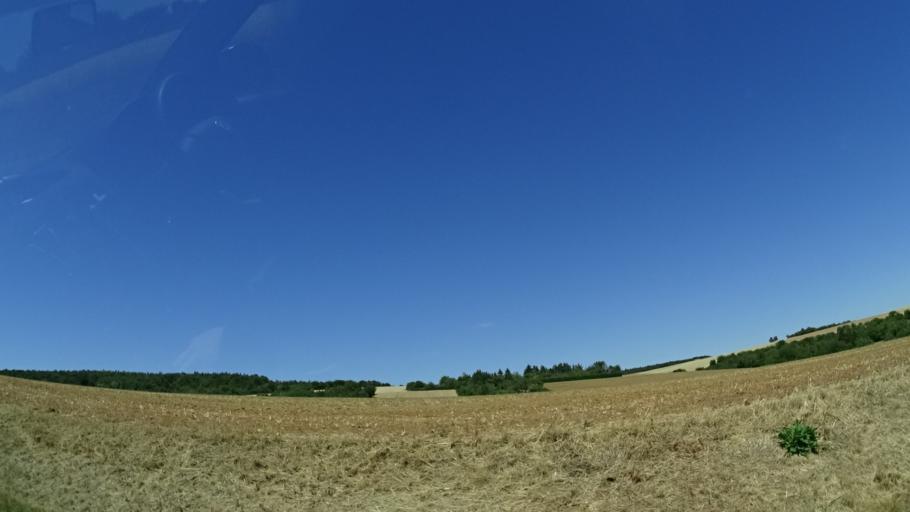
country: DE
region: Bavaria
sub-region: Regierungsbezirk Unterfranken
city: Rimpar
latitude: 49.8618
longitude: 9.9406
